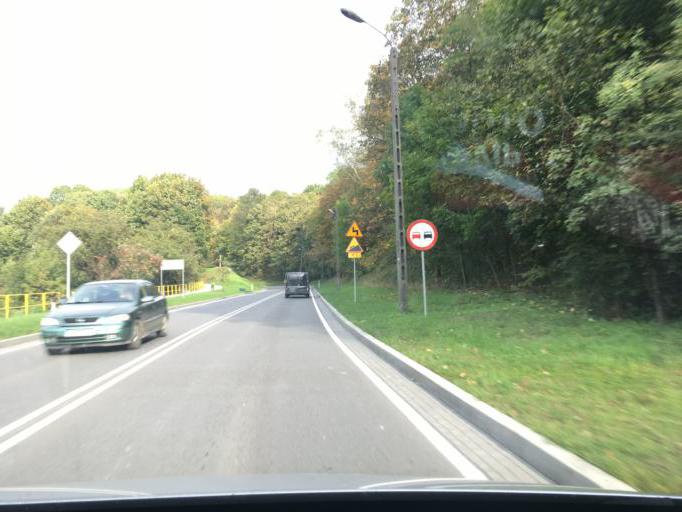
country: PL
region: Swietokrzyskie
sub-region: Powiat pinczowski
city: Pinczow
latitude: 50.5228
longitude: 20.5303
